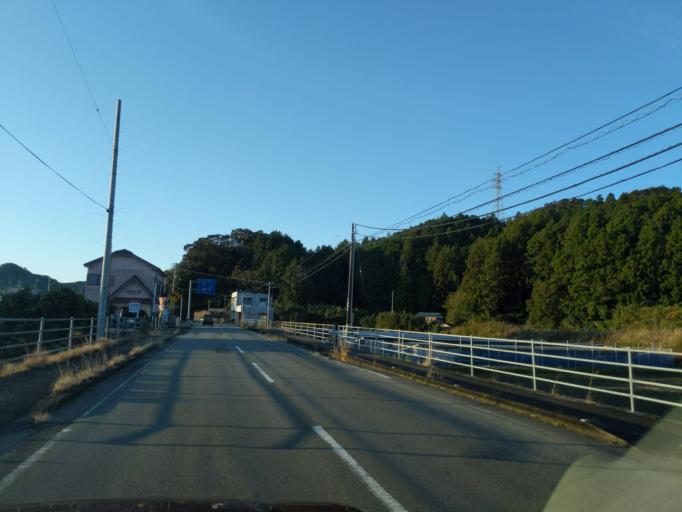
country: JP
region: Kochi
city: Muroto-misakicho
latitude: 33.6058
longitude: 134.3513
